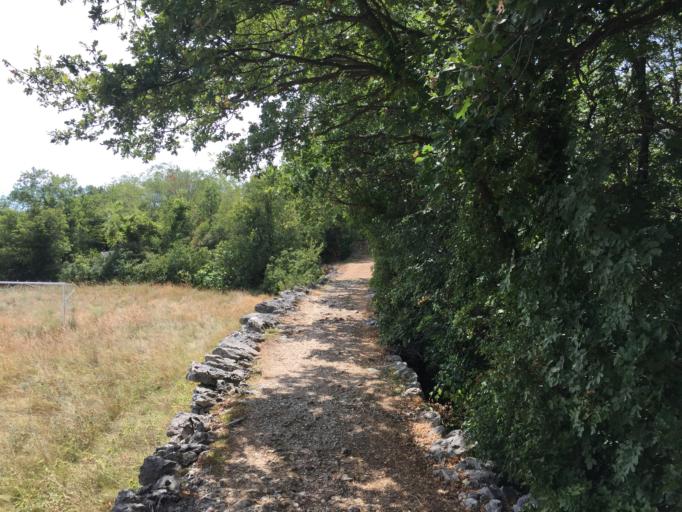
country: HR
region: Istarska
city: Lovran
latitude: 45.1810
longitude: 14.2383
